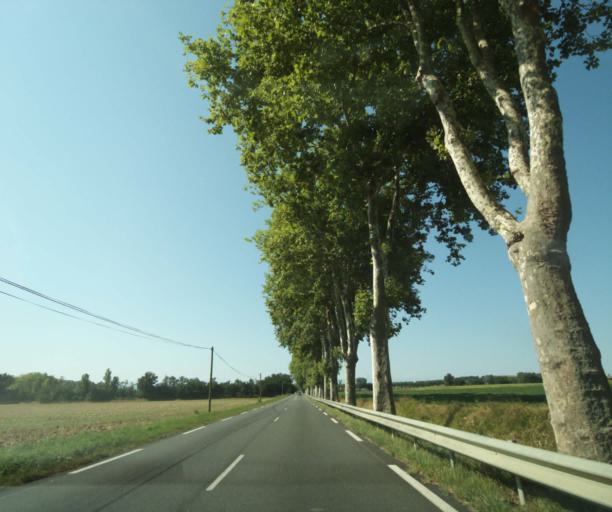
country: FR
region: Midi-Pyrenees
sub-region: Departement de la Haute-Garonne
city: Saint-Sulpice-sur-Leze
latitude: 43.3534
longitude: 1.3262
